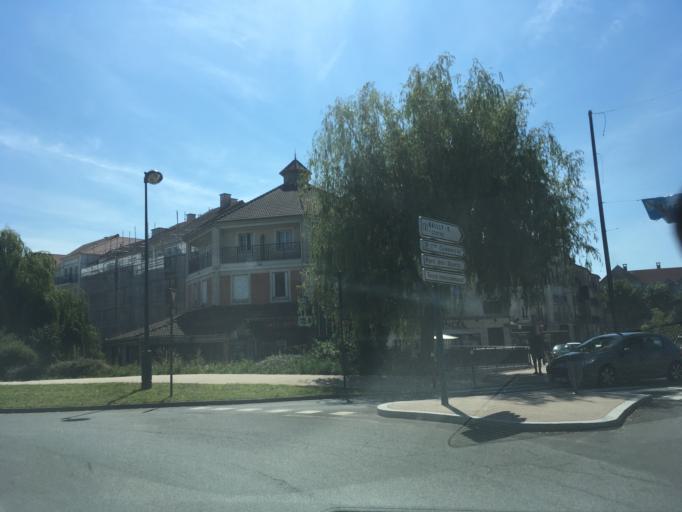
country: FR
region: Ile-de-France
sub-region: Departement de Seine-et-Marne
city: Bailly-Romainvilliers
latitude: 48.8510
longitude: 2.8191
